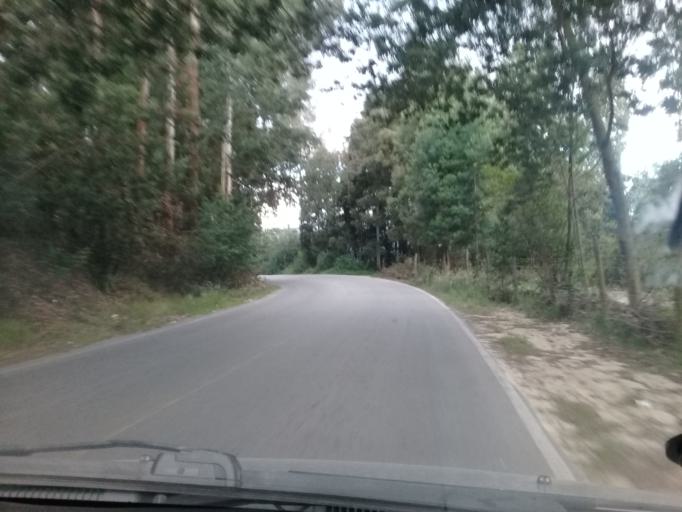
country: CO
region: Cundinamarca
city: Tabio
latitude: 4.9350
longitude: -74.1146
